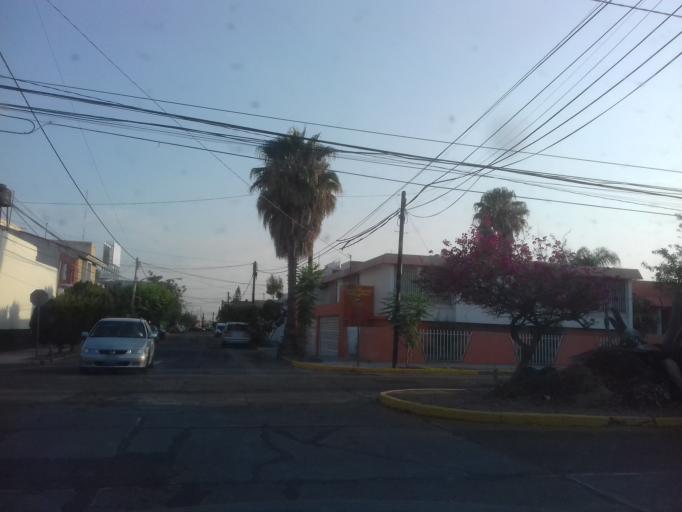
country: MX
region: Aguascalientes
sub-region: Aguascalientes
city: Aguascalientes
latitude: 21.8641
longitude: -102.2892
